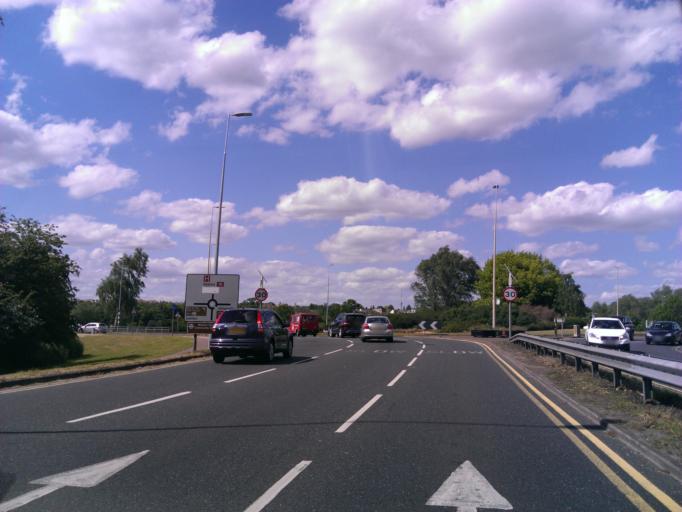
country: GB
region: England
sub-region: Essex
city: Colchester
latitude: 51.8960
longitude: 0.8913
